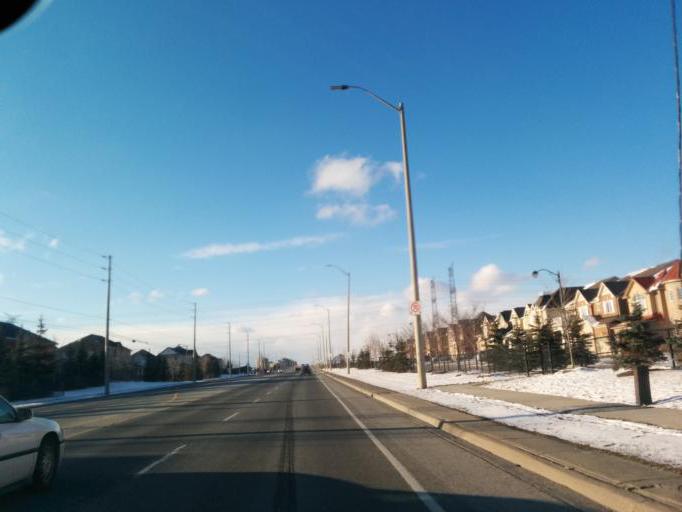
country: CA
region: Ontario
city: Brampton
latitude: 43.6418
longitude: -79.7237
